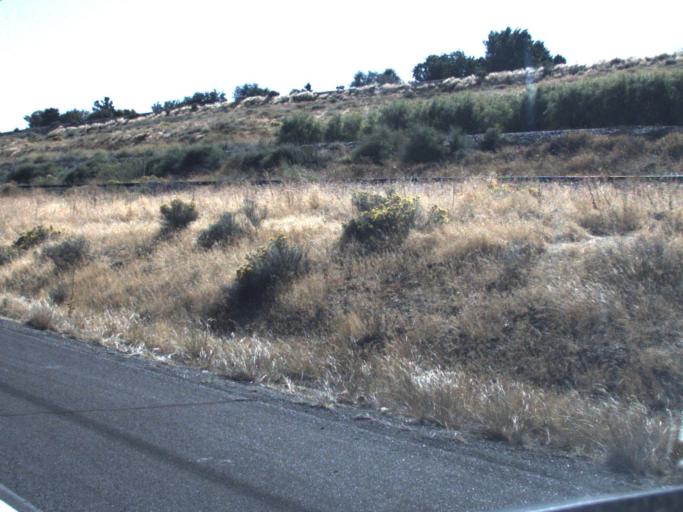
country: US
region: Washington
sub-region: Benton County
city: Kennewick
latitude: 46.2212
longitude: -119.1571
